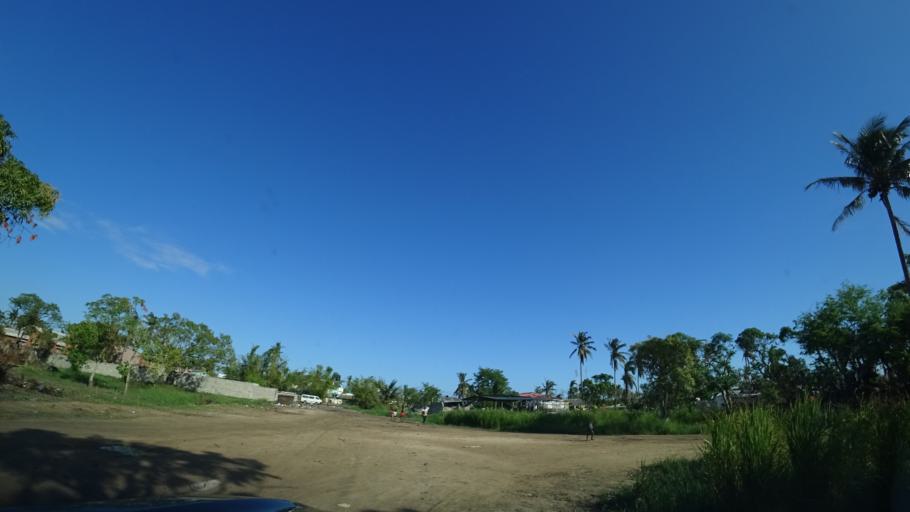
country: MZ
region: Sofala
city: Beira
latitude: -19.7524
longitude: 34.8693
